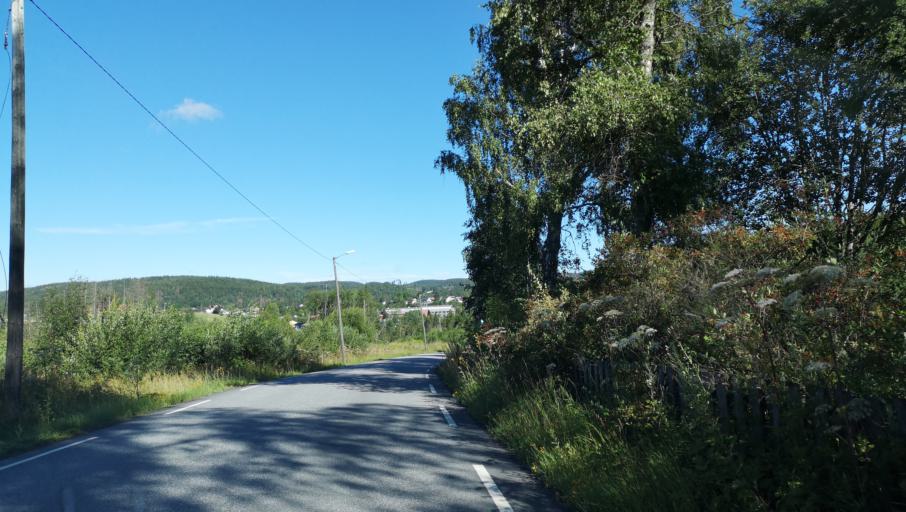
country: NO
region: Ostfold
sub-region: Hobol
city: Tomter
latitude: 59.6533
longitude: 11.0096
